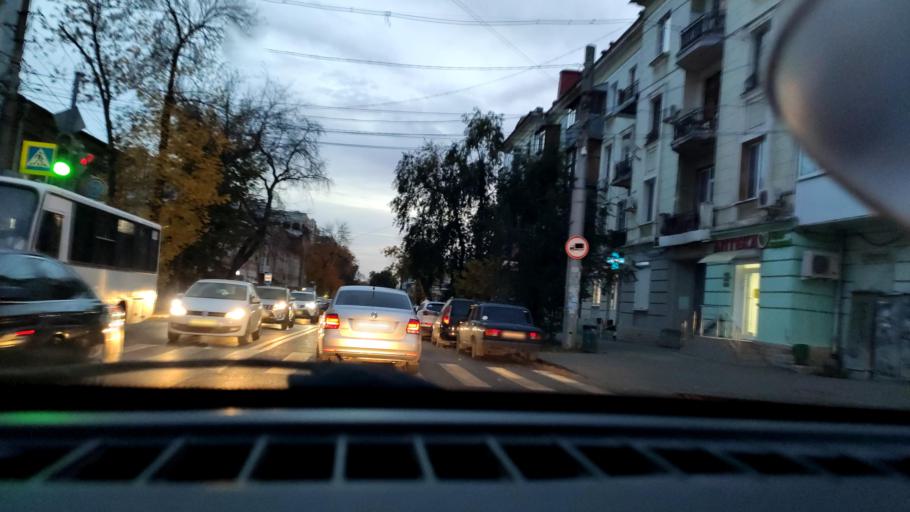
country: RU
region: Samara
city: Samara
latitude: 53.1853
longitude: 50.1002
